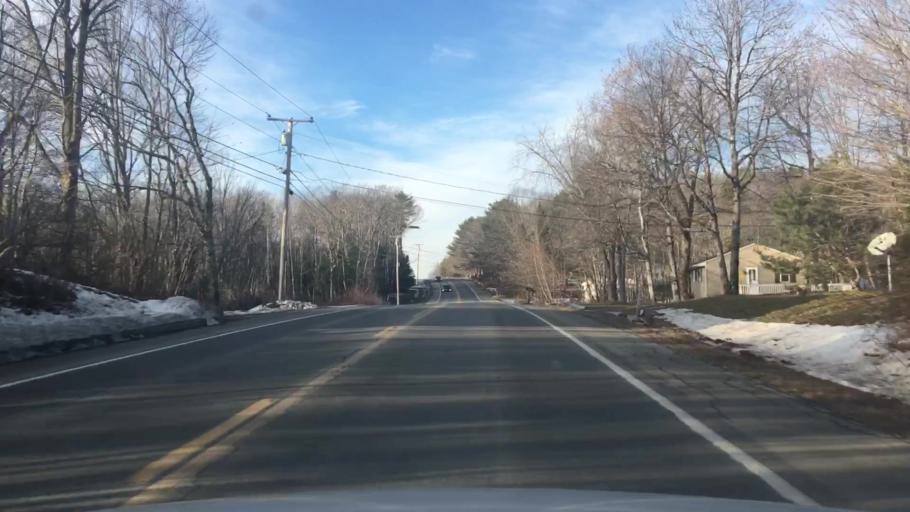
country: US
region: Maine
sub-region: Lincoln County
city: Wiscasset
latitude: 44.0455
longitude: -69.6776
